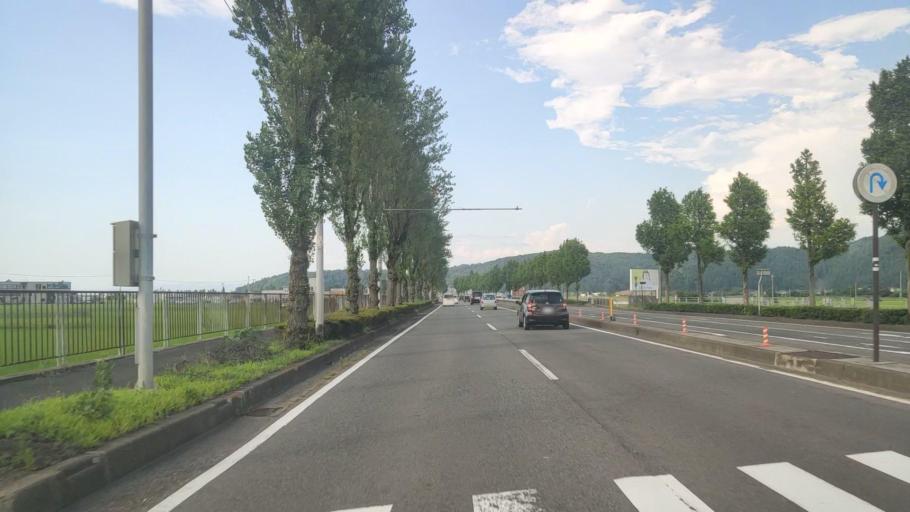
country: JP
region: Fukui
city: Sabae
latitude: 35.9909
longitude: 136.2015
